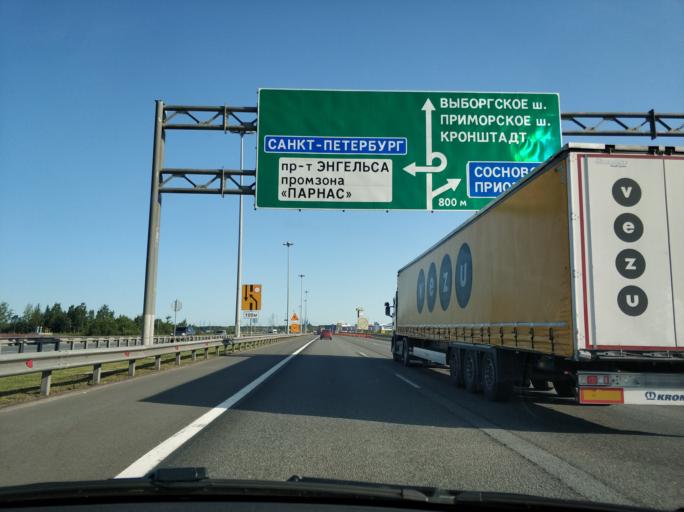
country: RU
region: Leningrad
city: Bugry
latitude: 60.0808
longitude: 30.3797
